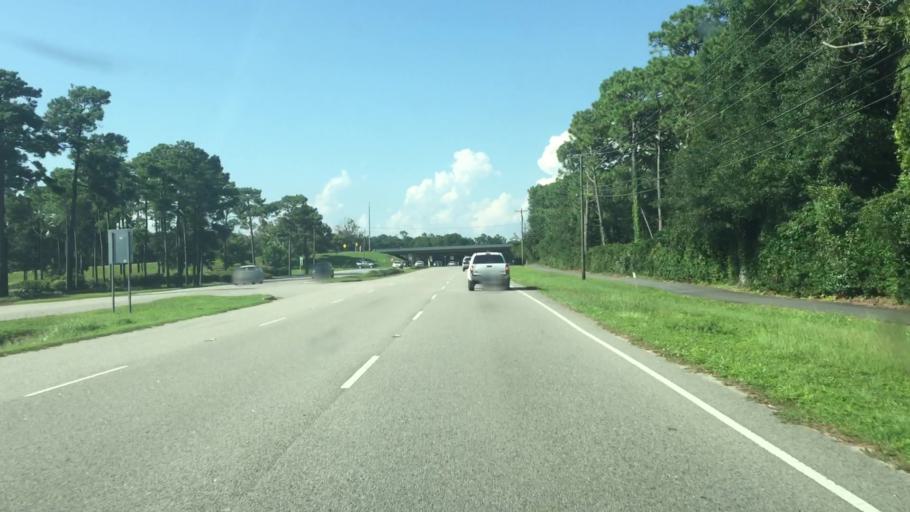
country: US
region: South Carolina
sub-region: Horry County
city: Myrtle Beach
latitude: 33.7645
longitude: -78.8058
